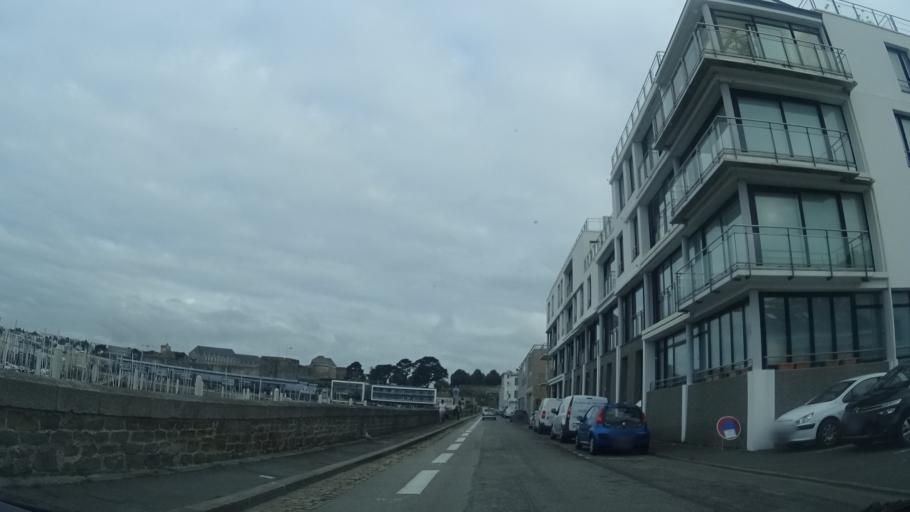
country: FR
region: Brittany
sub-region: Departement du Finistere
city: Brest
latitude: 48.3794
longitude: -4.4869
